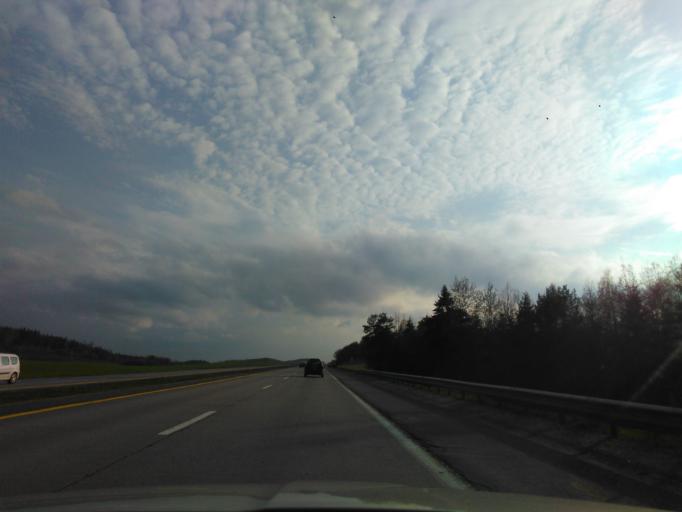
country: BY
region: Minsk
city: Astrashytski Haradok
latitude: 54.0755
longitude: 27.7354
